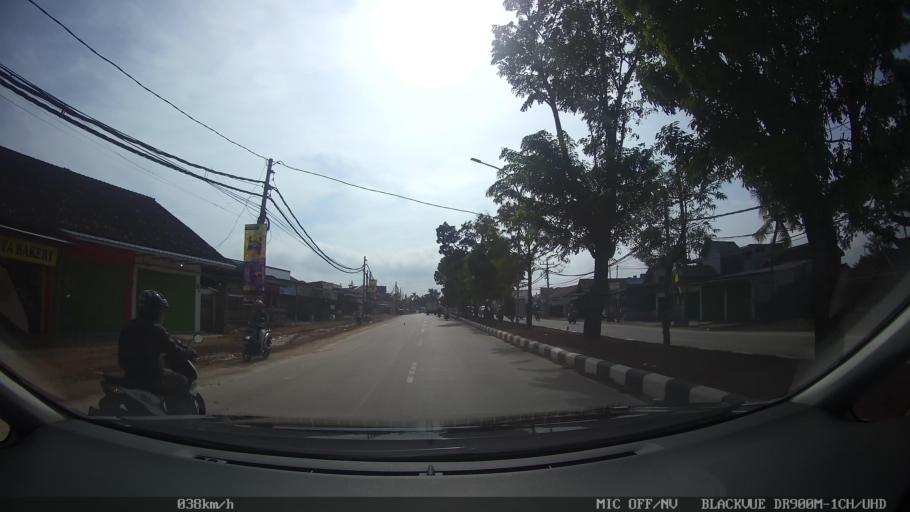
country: ID
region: Lampung
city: Kedaton
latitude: -5.3802
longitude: 105.2895
